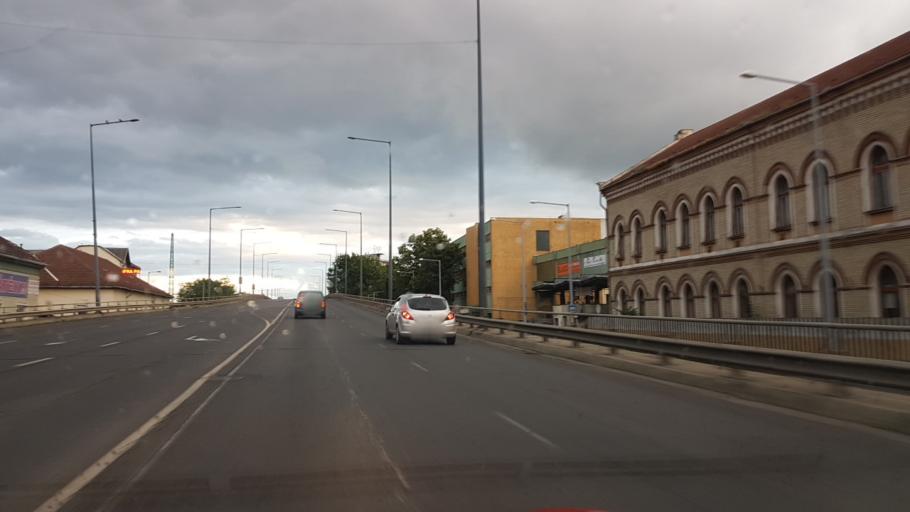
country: HU
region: Borsod-Abauj-Zemplen
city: Miskolc
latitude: 48.1045
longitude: 20.7982
